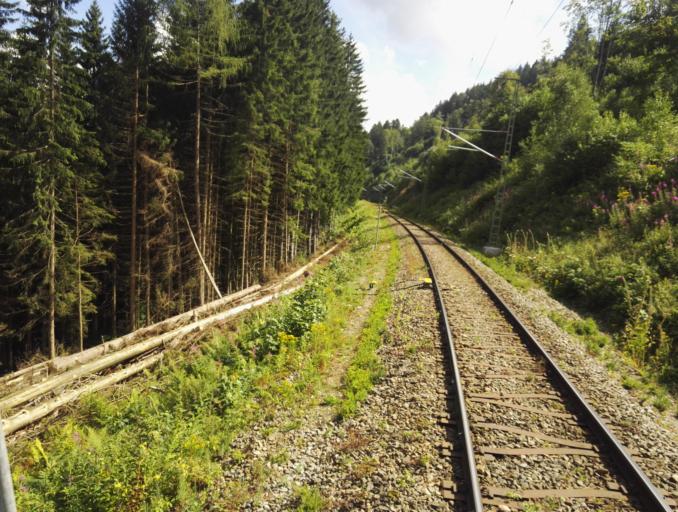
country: DE
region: Baden-Wuerttemberg
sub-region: Freiburg Region
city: Hinterzarten
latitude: 47.8746
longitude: 8.1081
